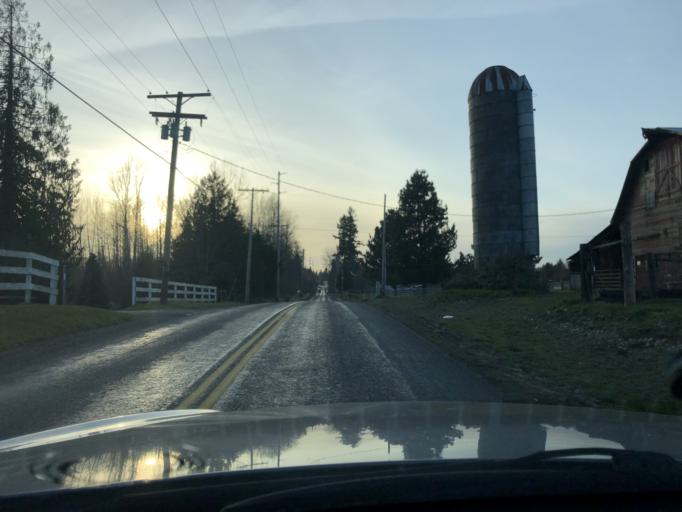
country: US
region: Washington
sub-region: Pierce County
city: Bonney Lake
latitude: 47.2211
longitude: -122.1271
